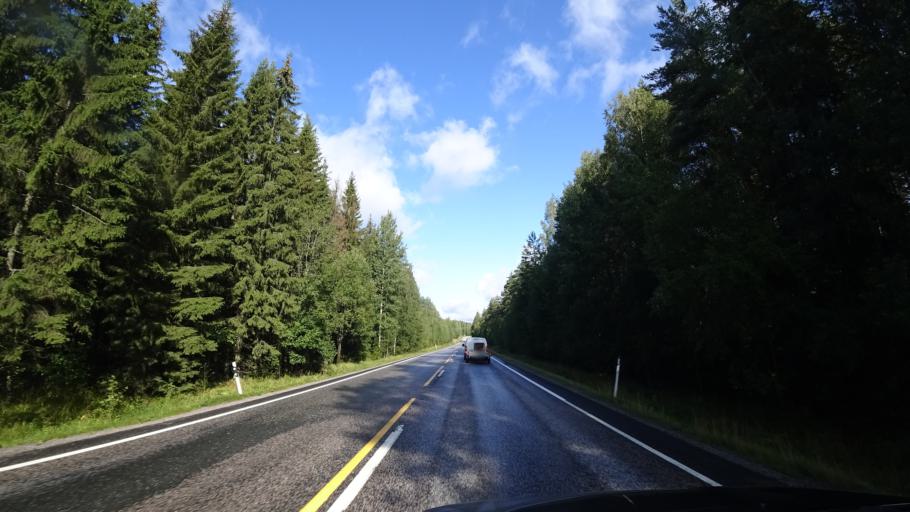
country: FI
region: Uusimaa
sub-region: Helsinki
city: Tuusula
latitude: 60.4544
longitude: 24.9542
